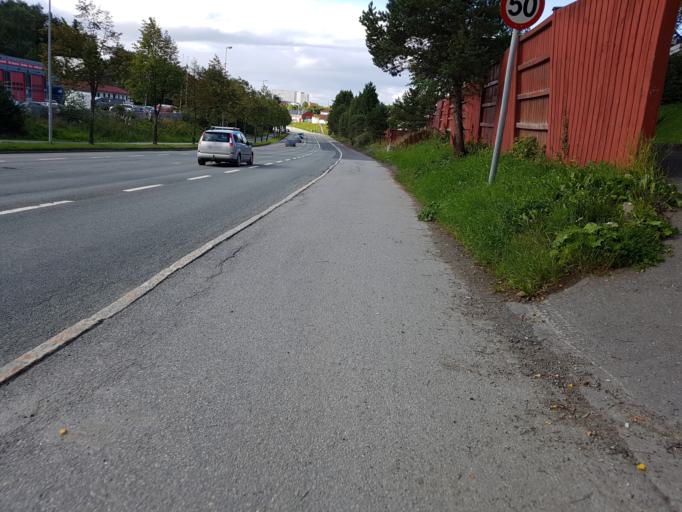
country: NO
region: Sor-Trondelag
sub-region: Trondheim
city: Trondheim
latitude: 63.4112
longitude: 10.4181
